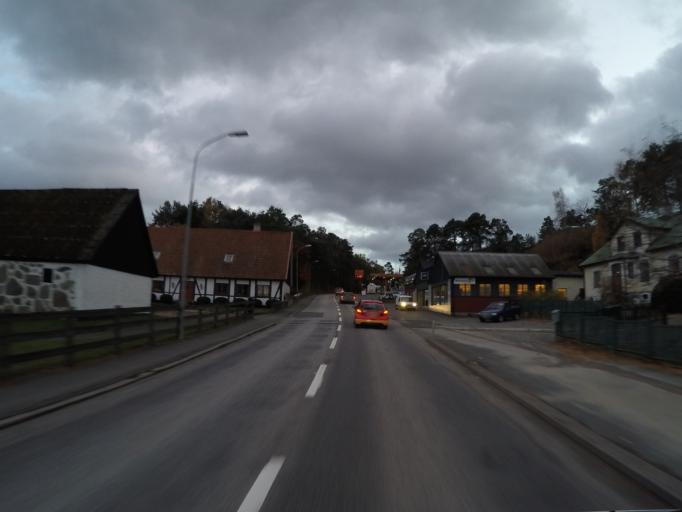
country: SE
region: Skane
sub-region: Kristianstads Kommun
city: Degeberga
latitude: 55.8352
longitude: 14.0903
